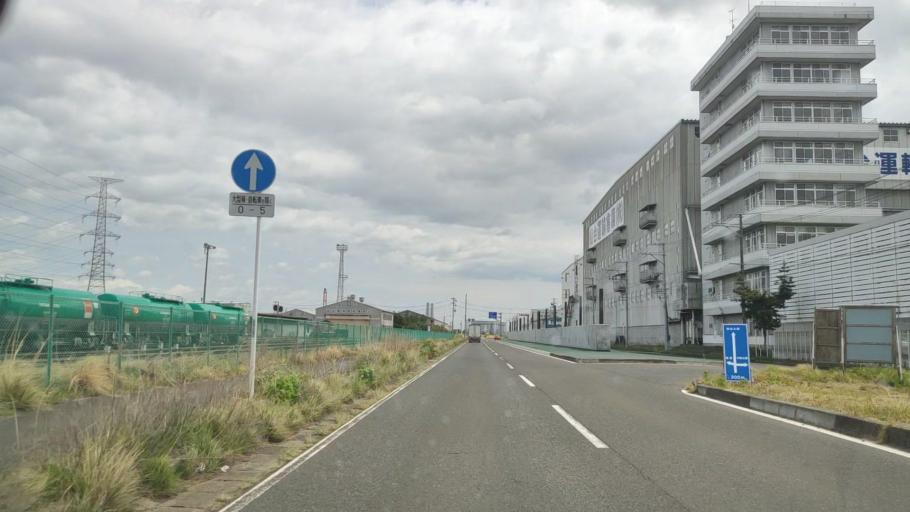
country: JP
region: Miyagi
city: Shiogama
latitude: 38.2763
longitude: 141.0146
